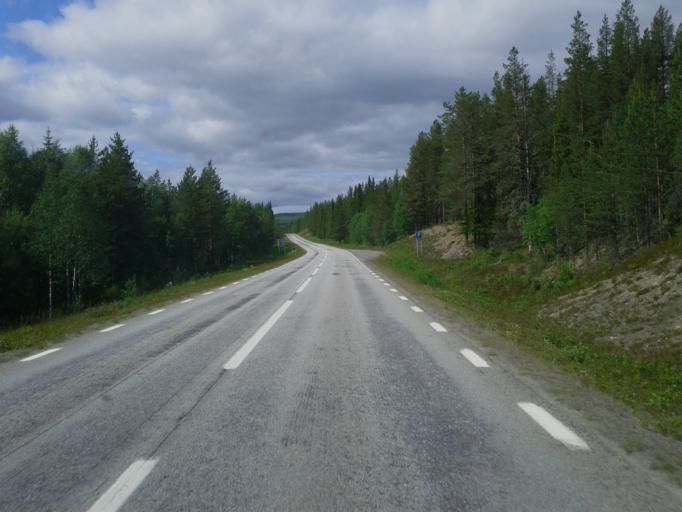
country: SE
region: Vaesterbotten
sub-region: Storumans Kommun
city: Fristad
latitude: 65.3854
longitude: 16.4849
